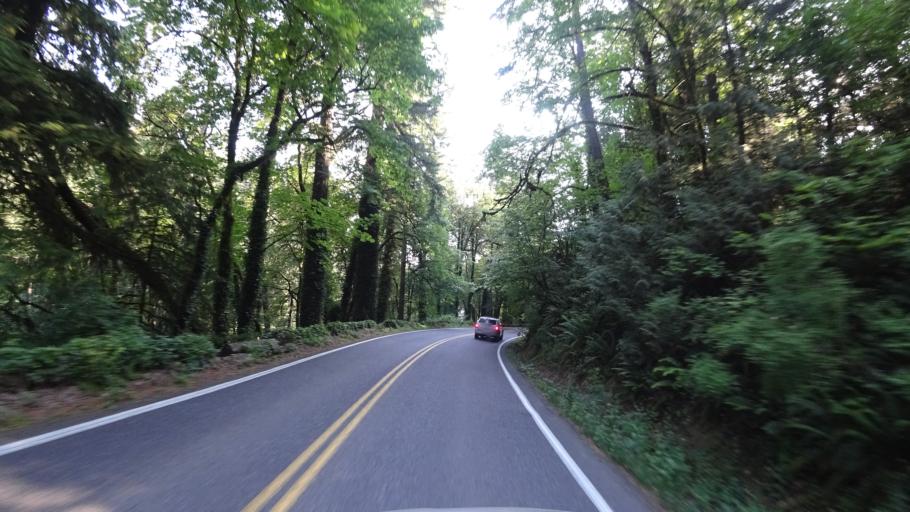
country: US
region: Oregon
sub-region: Washington County
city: Cedar Mill
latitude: 45.5885
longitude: -122.7851
